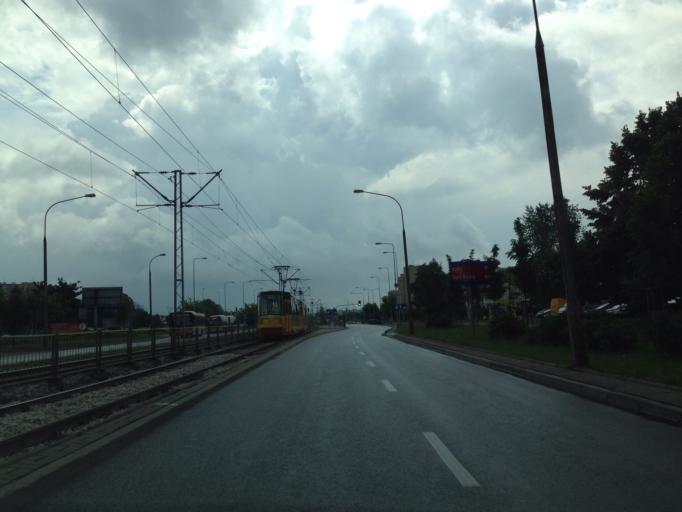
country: PL
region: Masovian Voivodeship
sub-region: Warszawa
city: Bemowo
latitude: 52.2498
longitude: 20.9184
